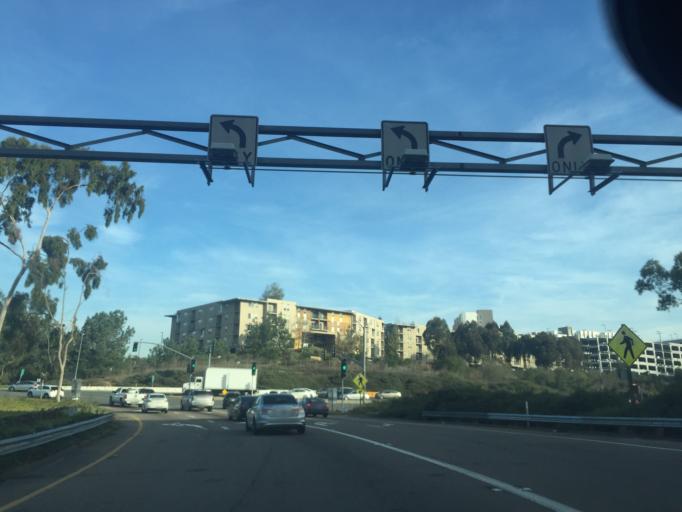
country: US
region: California
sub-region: San Diego County
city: La Jolla
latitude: 32.8716
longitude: -117.2277
